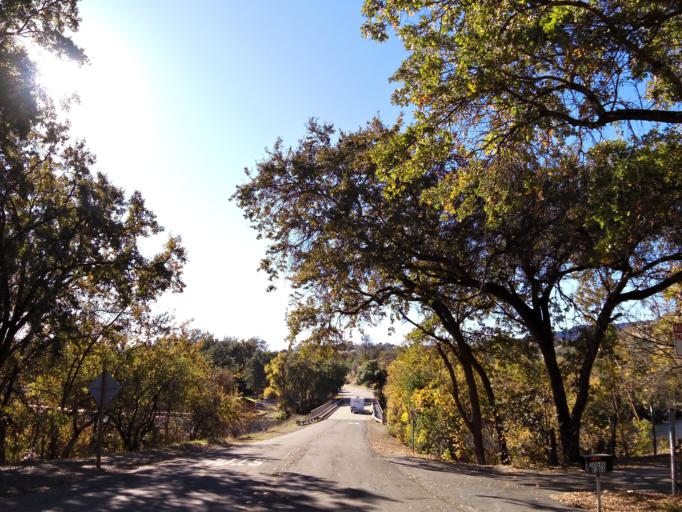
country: US
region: California
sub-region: Yolo County
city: Winters
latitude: 38.4943
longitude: -122.0278
